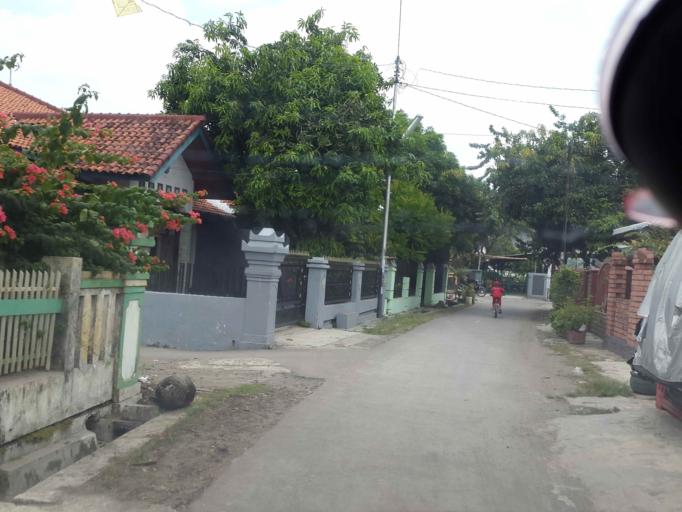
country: ID
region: Central Java
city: Slawi
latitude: -6.9821
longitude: 109.1474
